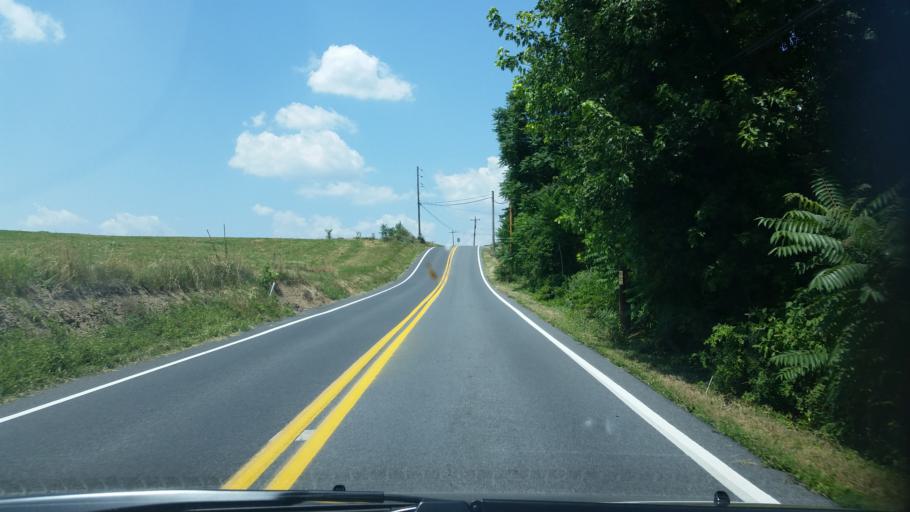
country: US
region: Pennsylvania
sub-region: Dauphin County
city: Rutherford
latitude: 40.2879
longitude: -76.7453
